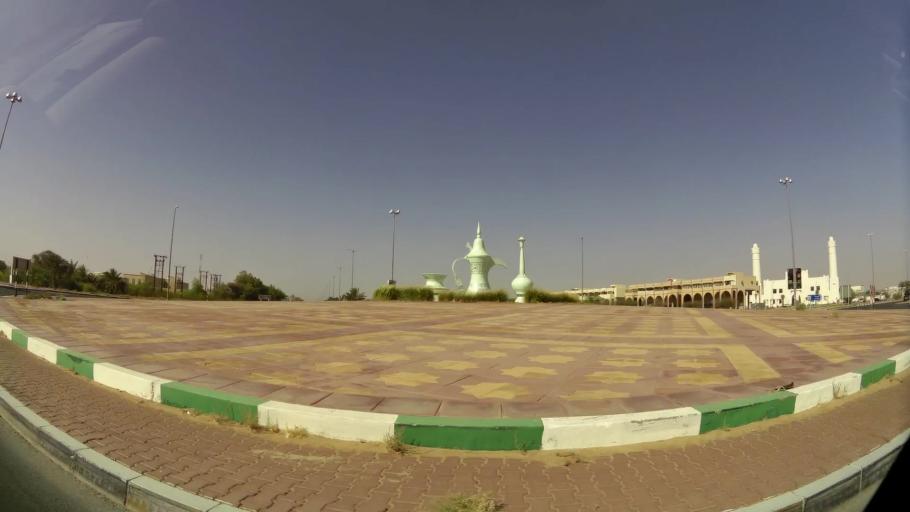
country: OM
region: Al Buraimi
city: Al Buraymi
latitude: 24.3397
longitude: 55.8057
